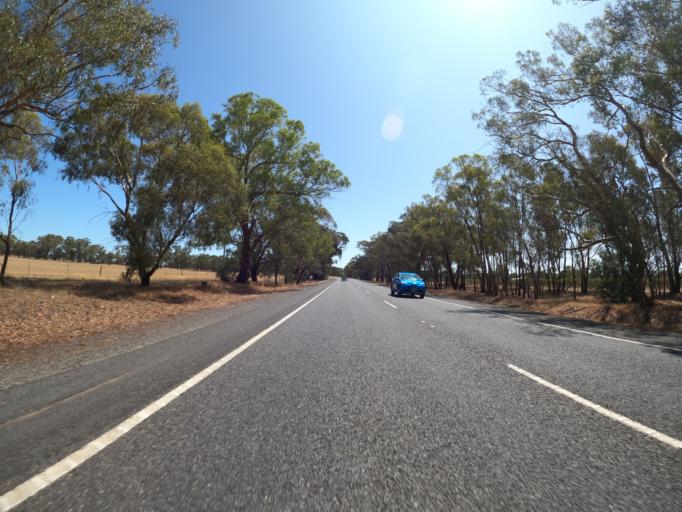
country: AU
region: New South Wales
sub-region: Corowa Shire
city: Corowa
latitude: -36.0627
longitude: 146.4001
